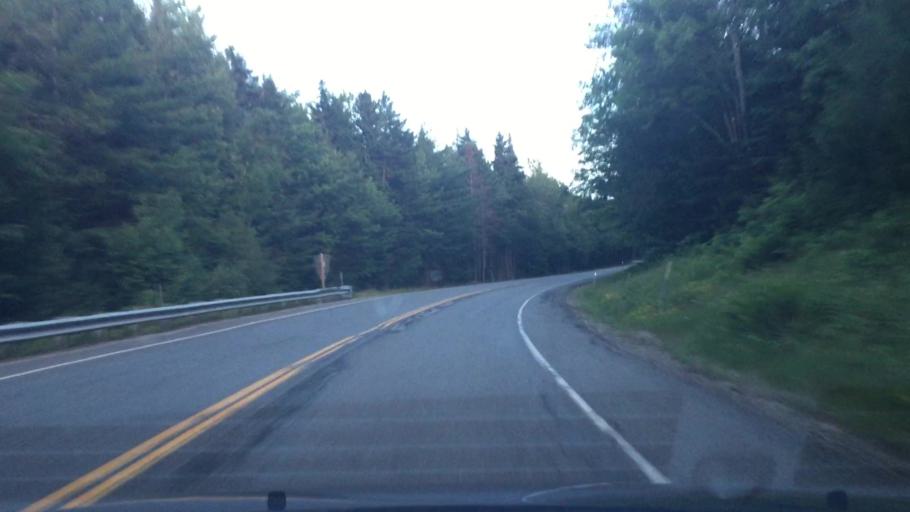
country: US
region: New Hampshire
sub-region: Grafton County
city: Woodstock
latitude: 44.0348
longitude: -71.5282
